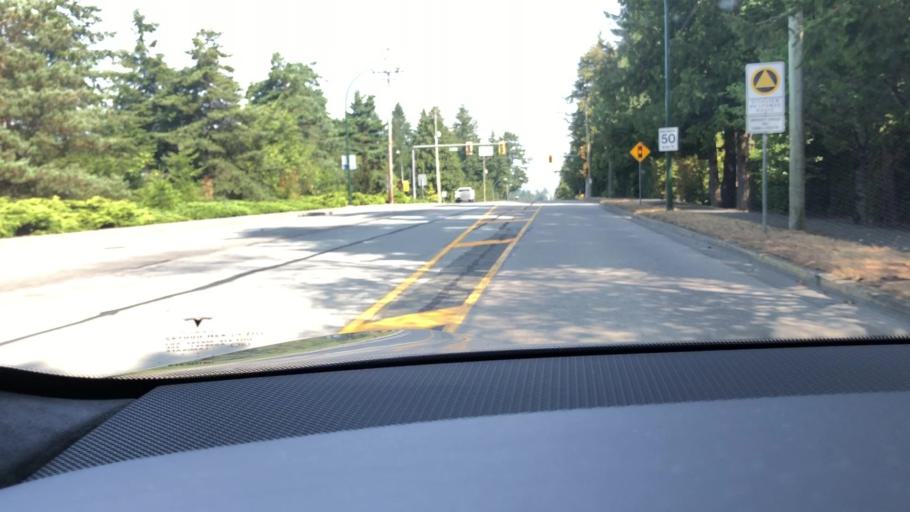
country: US
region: Washington
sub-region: Whatcom County
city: Point Roberts
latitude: 49.0035
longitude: -123.0686
